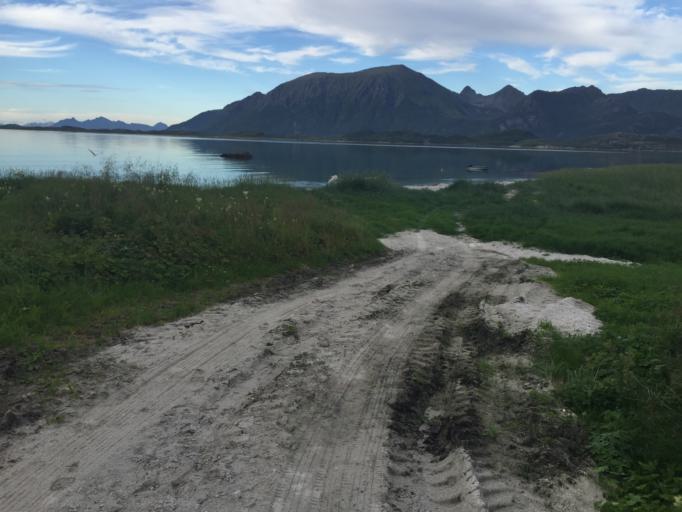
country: NO
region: Nordland
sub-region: Vagan
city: Kabelvag
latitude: 68.3288
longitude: 14.3967
